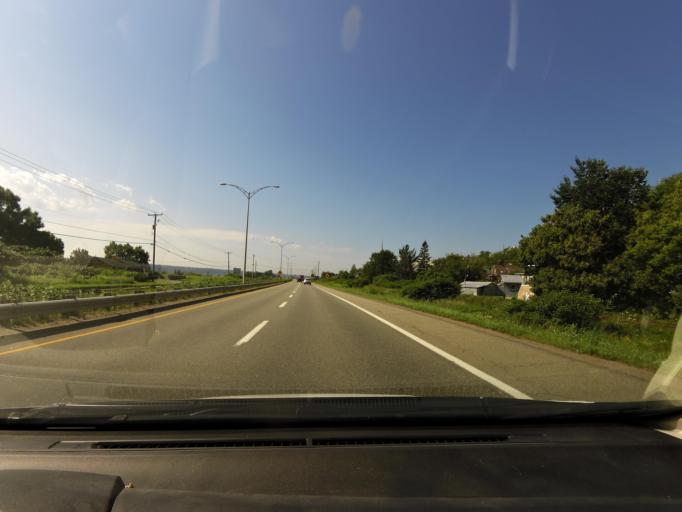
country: CA
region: Quebec
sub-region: Capitale-Nationale
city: Chateau-Richer
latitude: 46.9739
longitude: -71.0137
